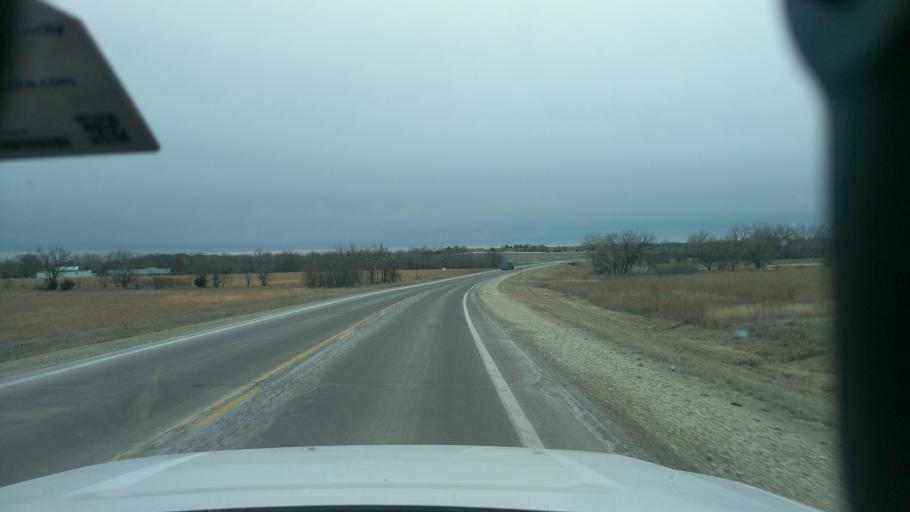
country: US
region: Kansas
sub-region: Dickinson County
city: Herington
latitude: 38.6582
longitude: -96.9330
